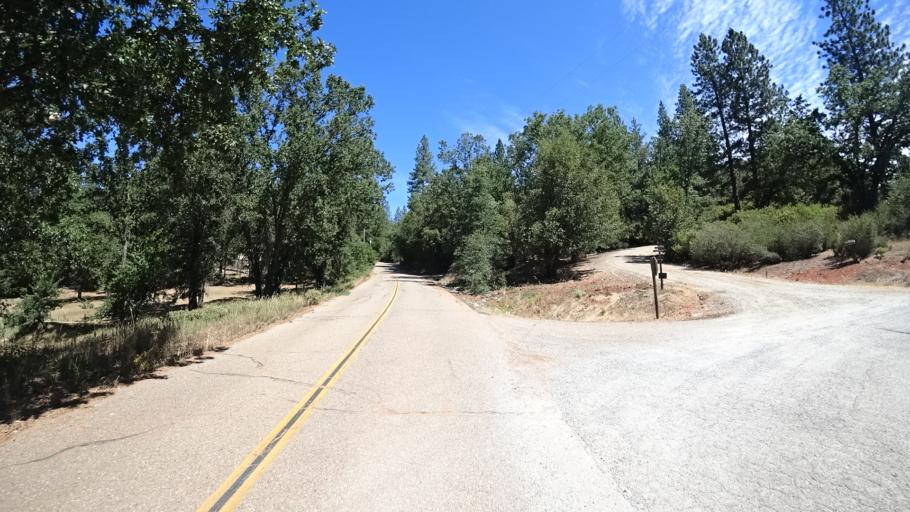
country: US
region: California
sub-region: Amador County
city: Pioneer
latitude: 38.3550
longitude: -120.5198
